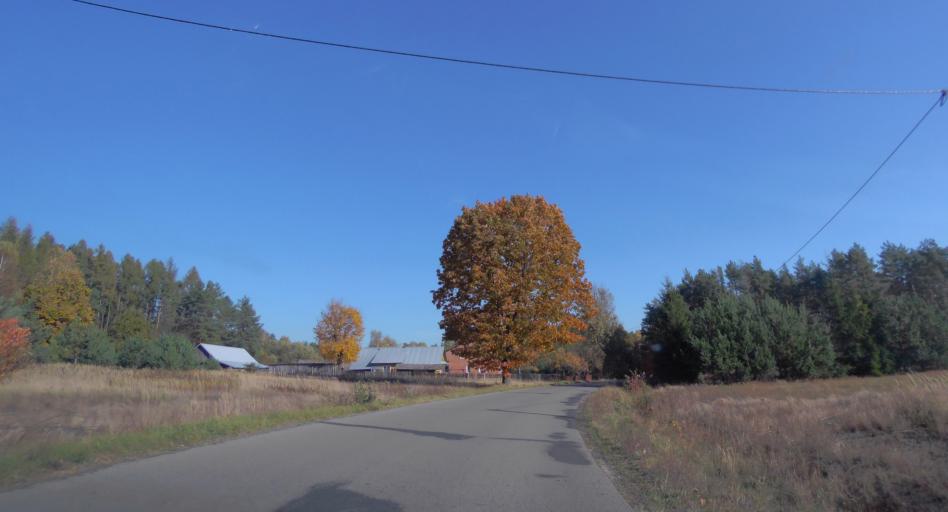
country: PL
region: Subcarpathian Voivodeship
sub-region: Powiat lezajski
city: Wola Zarczycka
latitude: 50.2636
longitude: 22.2419
